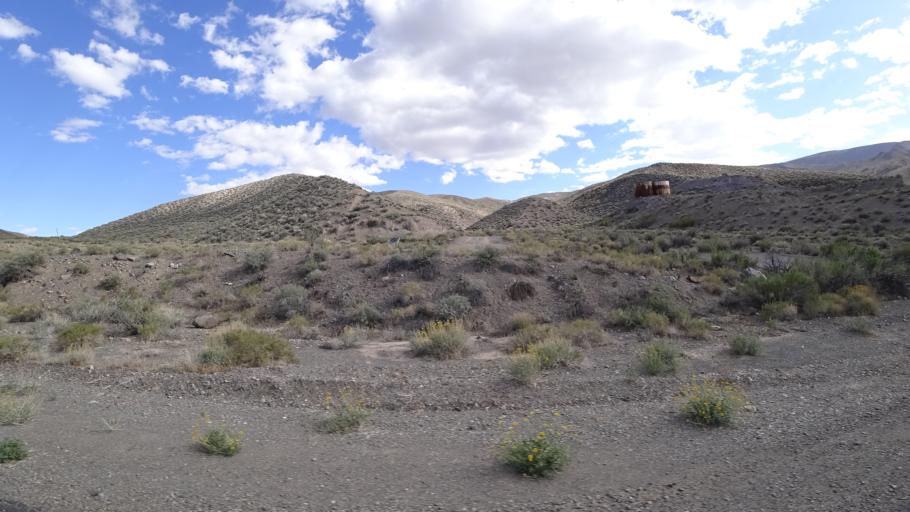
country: US
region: Nevada
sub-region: Nye County
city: Beatty
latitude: 36.4139
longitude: -117.1817
